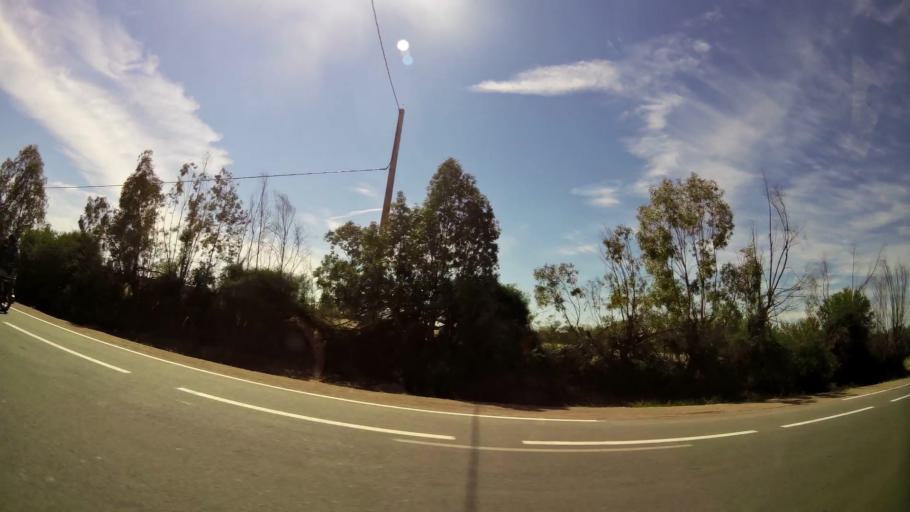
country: MA
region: Marrakech-Tensift-Al Haouz
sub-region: Marrakech
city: Marrakesh
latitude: 31.6574
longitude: -8.1053
